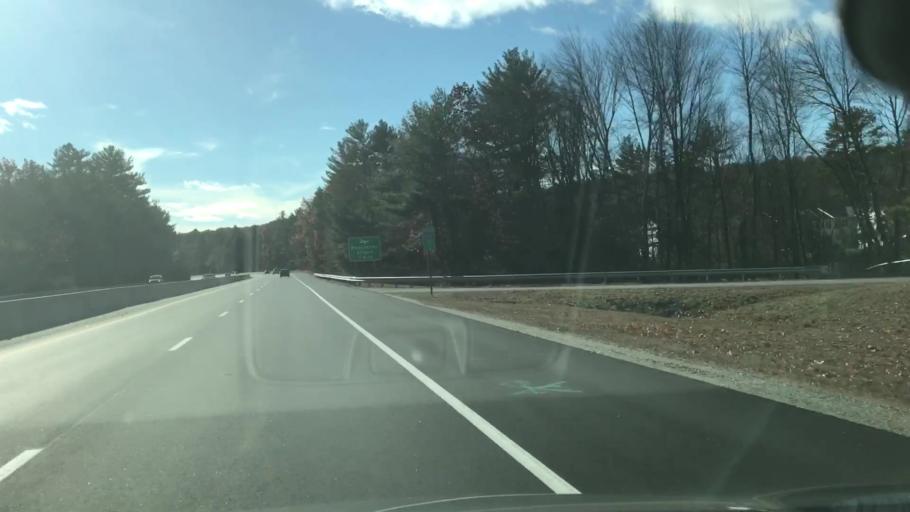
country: US
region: New Hampshire
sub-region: Merrimack County
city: South Hooksett
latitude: 43.0380
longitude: -71.4821
